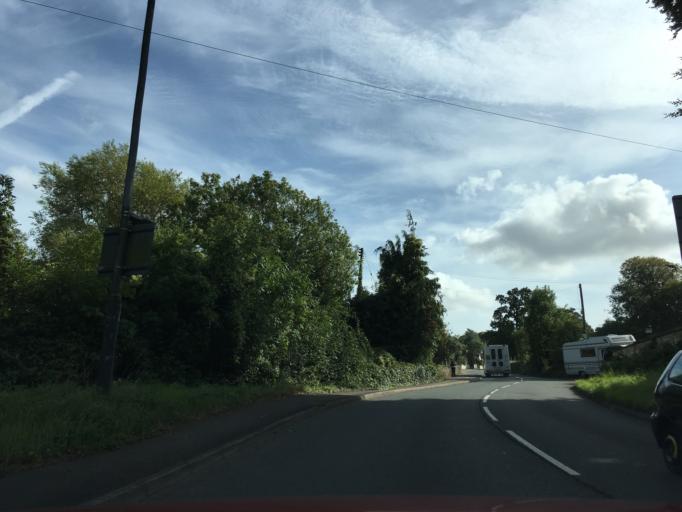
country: GB
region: England
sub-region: Gloucestershire
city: Stroud
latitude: 51.7383
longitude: -2.2411
